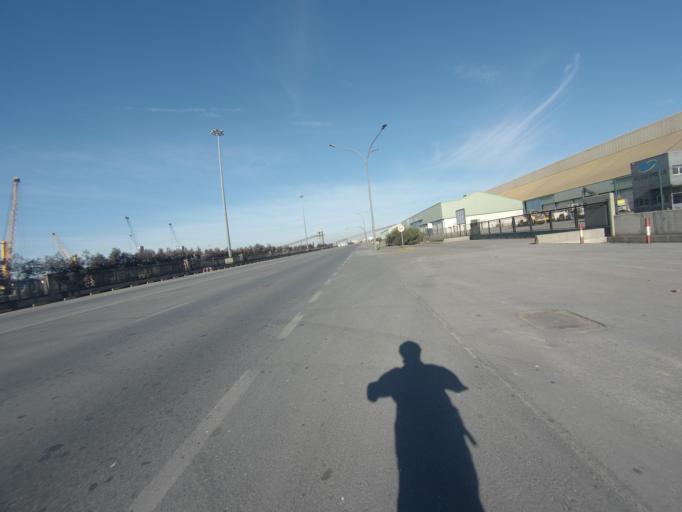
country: ES
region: Andalusia
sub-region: Provincia de Huelva
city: Punta Umbria
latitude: 37.1940
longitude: -6.9320
